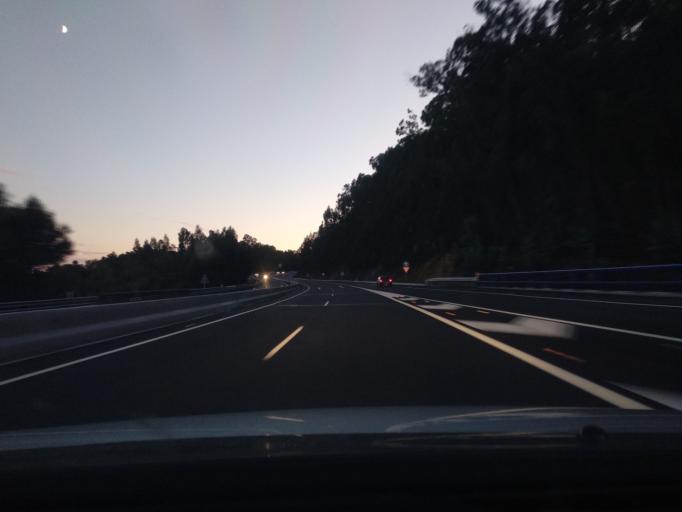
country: ES
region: Galicia
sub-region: Provincia de Pontevedra
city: Moana
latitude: 42.3041
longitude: -8.7436
